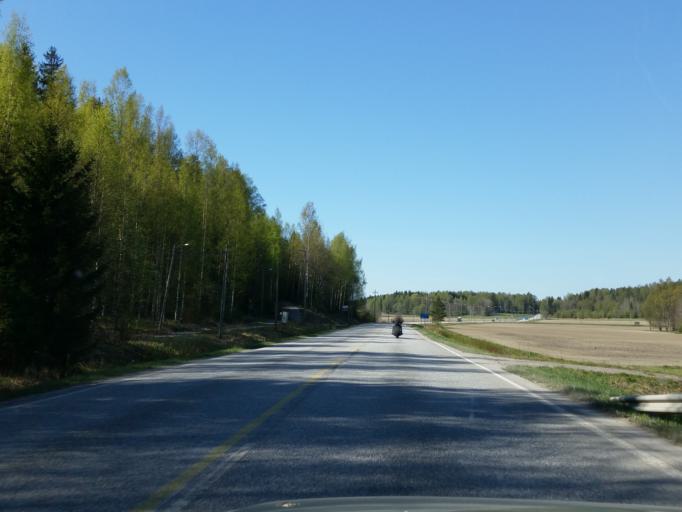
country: FI
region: Uusimaa
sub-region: Helsinki
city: Siuntio
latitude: 60.1755
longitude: 24.2157
